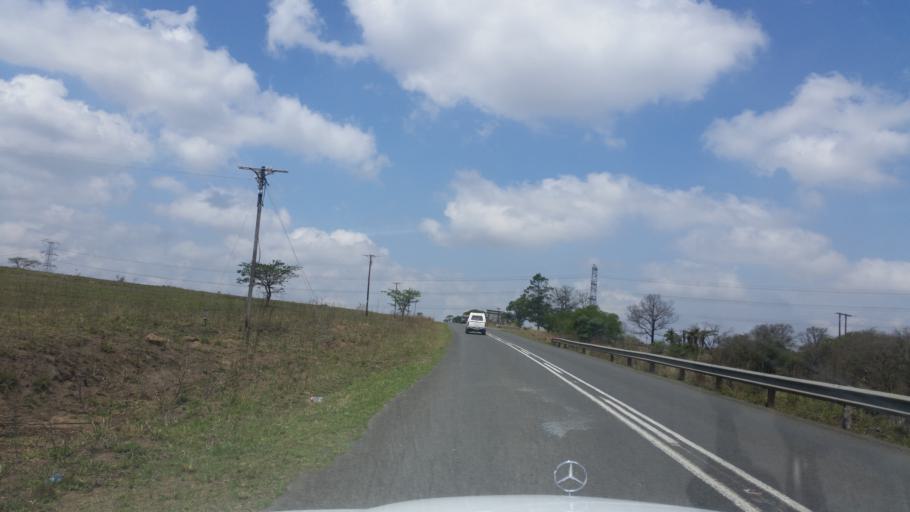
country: ZA
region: KwaZulu-Natal
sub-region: uMgungundlovu District Municipality
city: Camperdown
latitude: -29.6951
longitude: 30.4896
